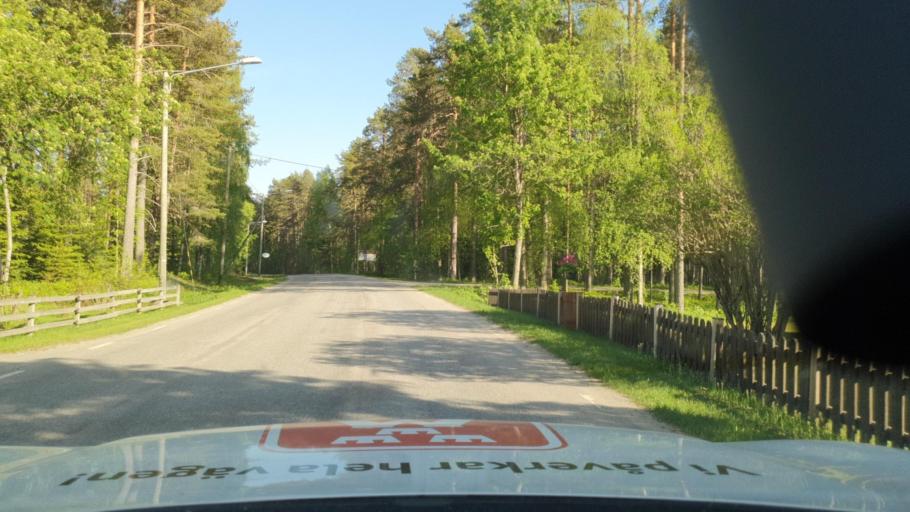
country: SE
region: Vaesterbotten
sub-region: Umea Kommun
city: Roback
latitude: 63.8450
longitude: 20.1202
